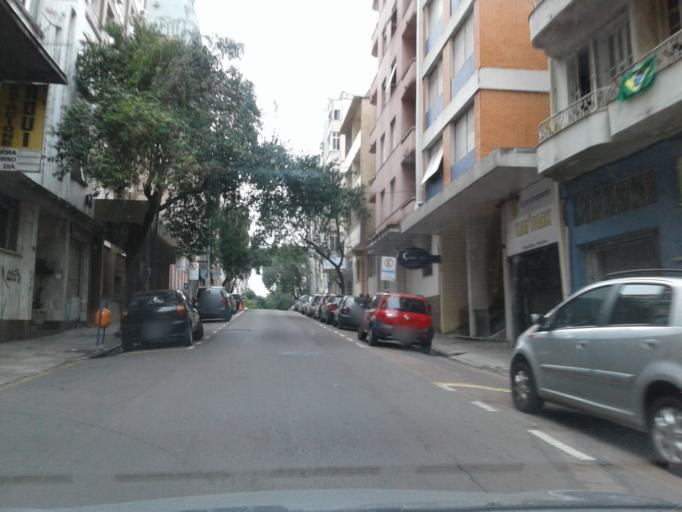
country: BR
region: Rio Grande do Sul
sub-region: Porto Alegre
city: Porto Alegre
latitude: -30.0320
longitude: -51.2320
